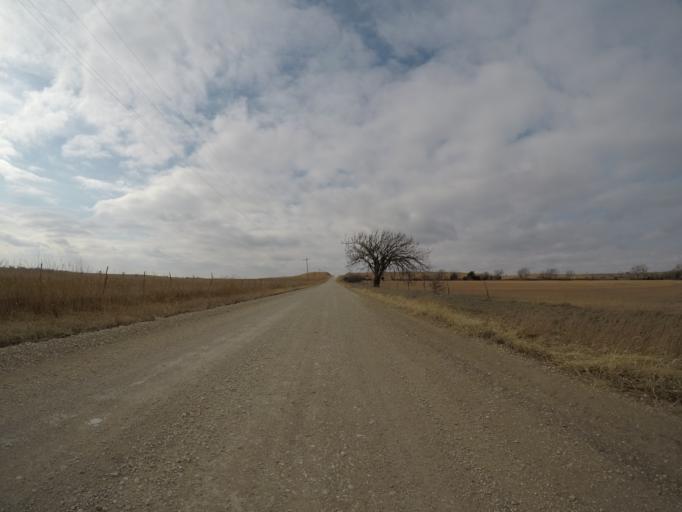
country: US
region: Kansas
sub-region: Morris County
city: Council Grove
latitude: 38.7680
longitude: -96.3183
